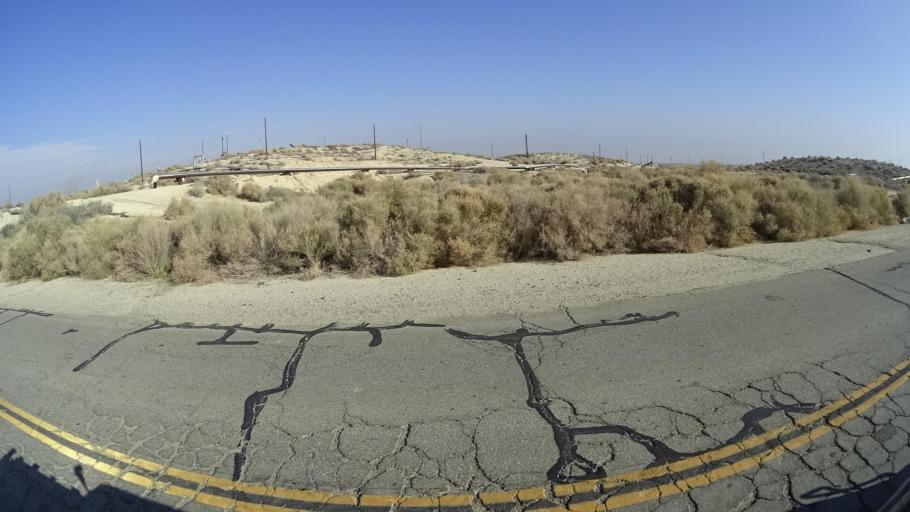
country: US
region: California
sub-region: Kern County
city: Taft Heights
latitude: 35.1575
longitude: -119.5219
